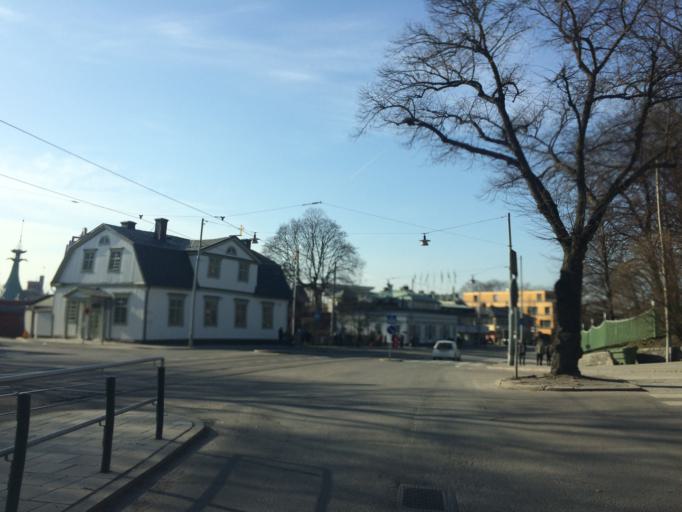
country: SE
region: Stockholm
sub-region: Stockholms Kommun
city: OEstermalm
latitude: 59.3242
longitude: 18.0994
